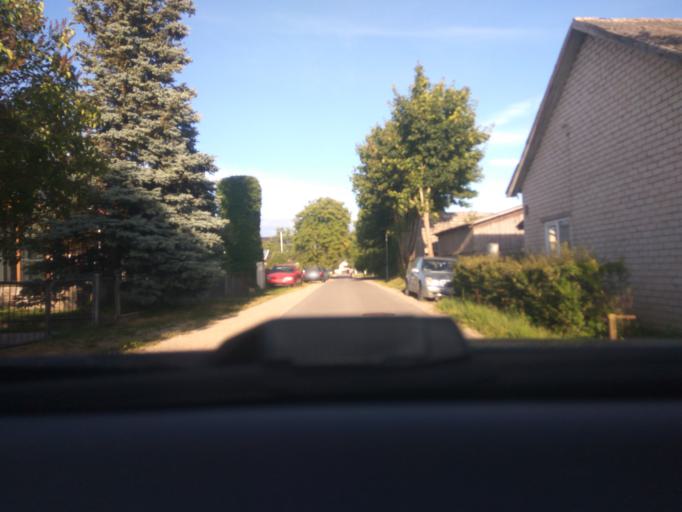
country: LV
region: Grobina
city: Grobina
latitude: 56.5317
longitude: 21.1751
